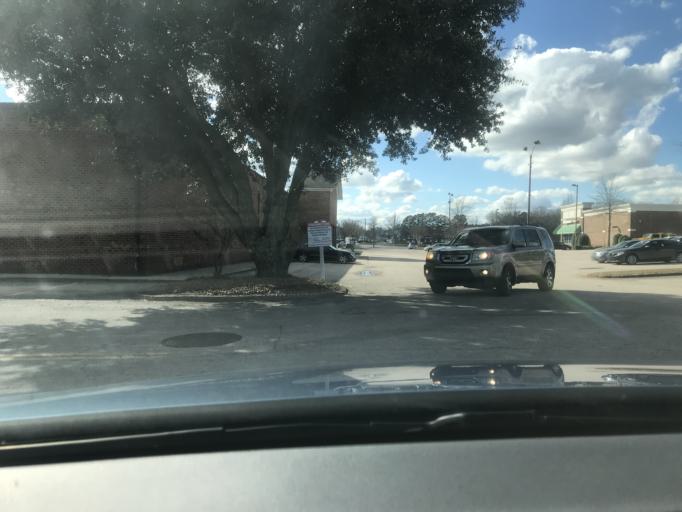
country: US
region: North Carolina
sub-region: Wake County
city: Cary
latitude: 35.7674
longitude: -78.7393
